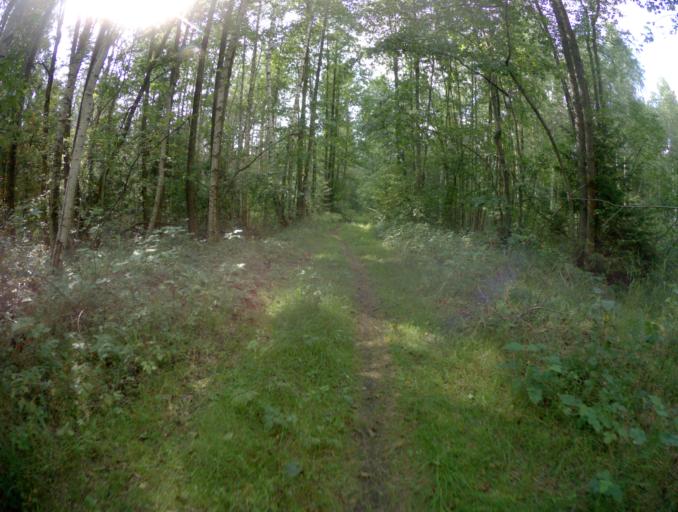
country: RU
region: Vladimir
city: Sobinka
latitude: 55.9145
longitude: 40.0998
